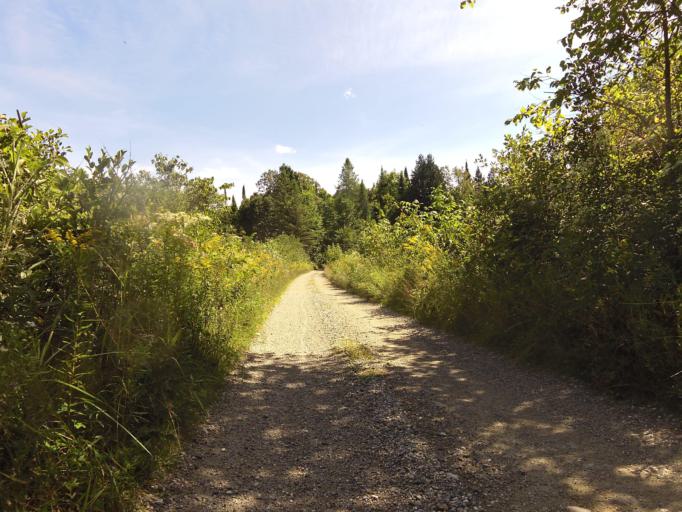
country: CA
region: Ontario
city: Renfrew
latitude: 45.0197
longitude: -76.7021
